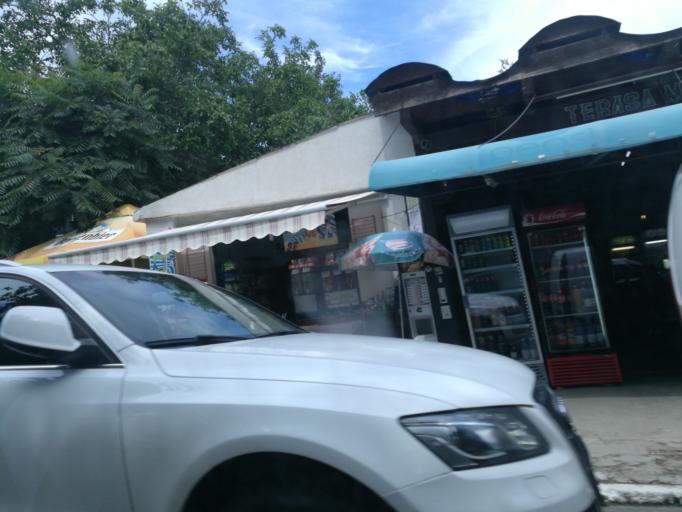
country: RO
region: Constanta
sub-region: Oras Eforie
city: Eforie Nord
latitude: 44.0653
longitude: 28.6363
